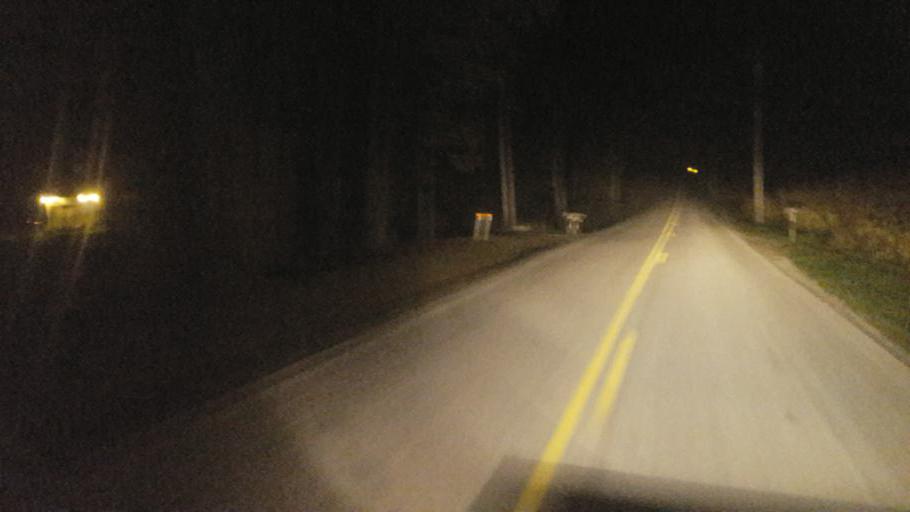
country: US
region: Ohio
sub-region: Richland County
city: Lexington
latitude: 40.6011
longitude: -82.6183
